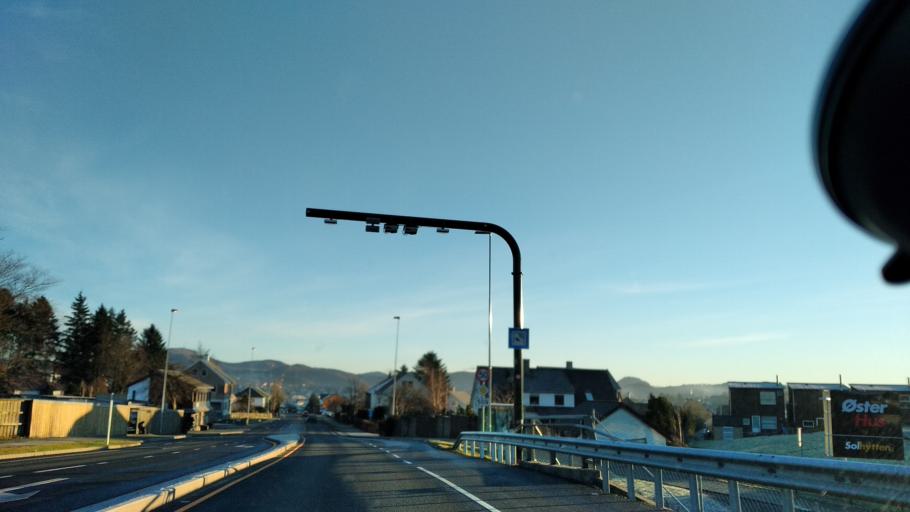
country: NO
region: Rogaland
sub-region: Sandnes
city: Sandnes
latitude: 58.8553
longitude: 5.7148
